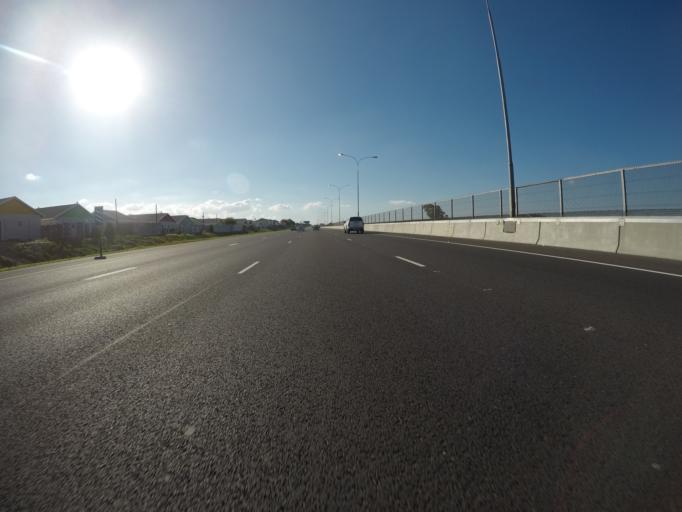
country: ZA
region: Western Cape
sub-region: City of Cape Town
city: Kraaifontein
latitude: -33.9630
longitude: 18.6556
